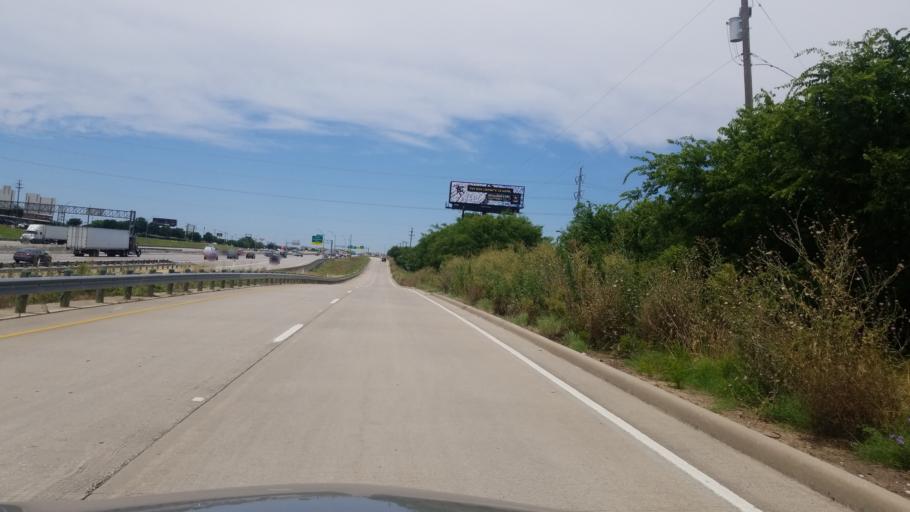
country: US
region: Texas
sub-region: Dallas County
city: Grand Prairie
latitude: 32.6765
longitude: -97.0320
